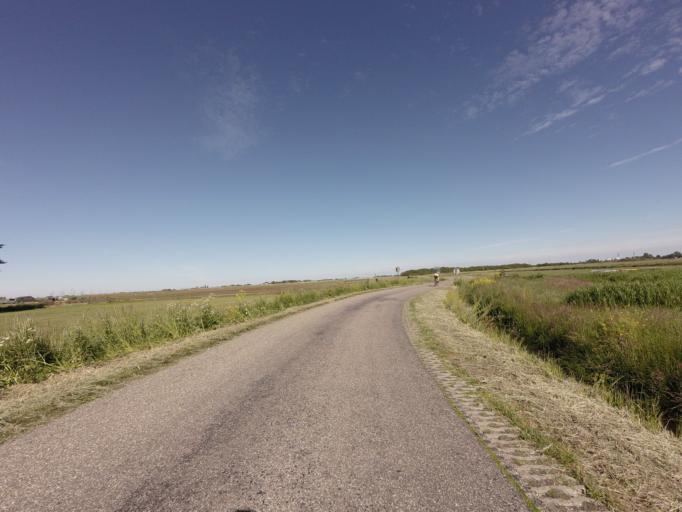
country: NL
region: North Holland
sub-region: Gemeente Uitgeest
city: Uitgeest
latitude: 52.5260
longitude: 4.7411
